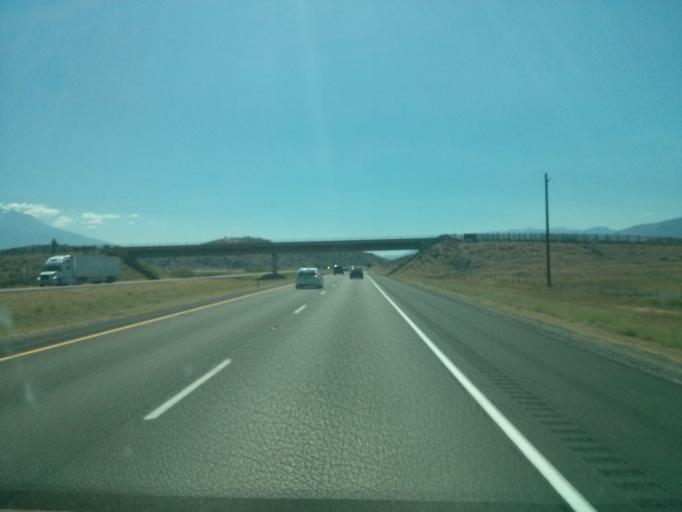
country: US
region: California
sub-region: Siskiyou County
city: Montague
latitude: 41.6039
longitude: -122.5087
